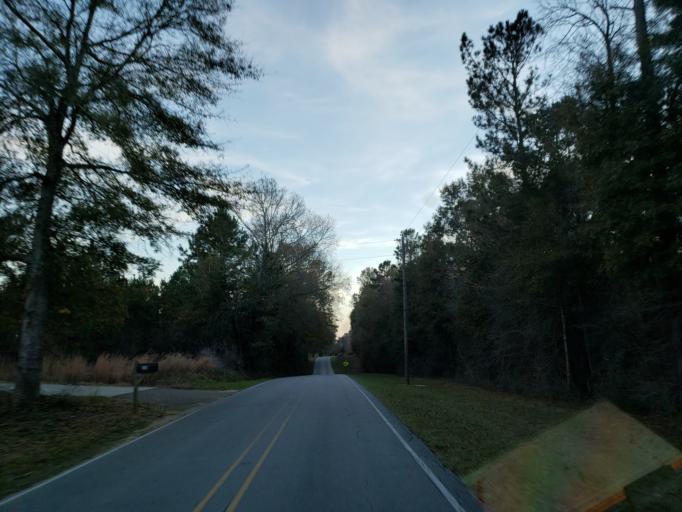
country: US
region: Mississippi
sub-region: Forrest County
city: Hattiesburg
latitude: 31.2468
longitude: -89.3140
